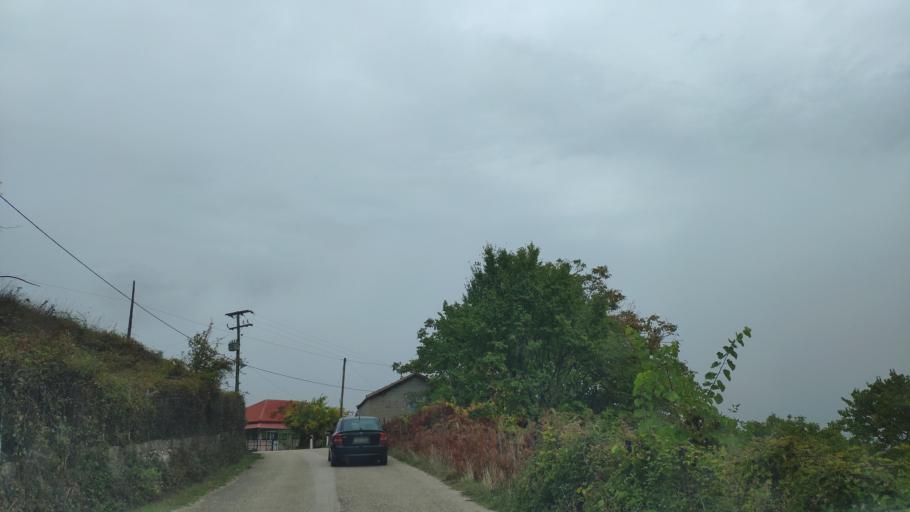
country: GR
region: Epirus
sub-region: Nomos Thesprotias
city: Paramythia
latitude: 39.4711
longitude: 20.6693
